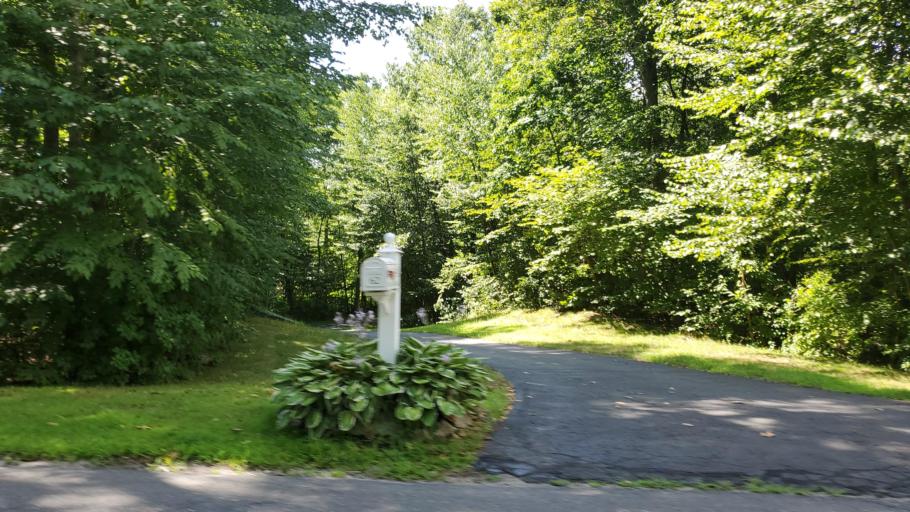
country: US
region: Connecticut
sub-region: Fairfield County
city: Newtown
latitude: 41.3475
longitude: -73.2764
